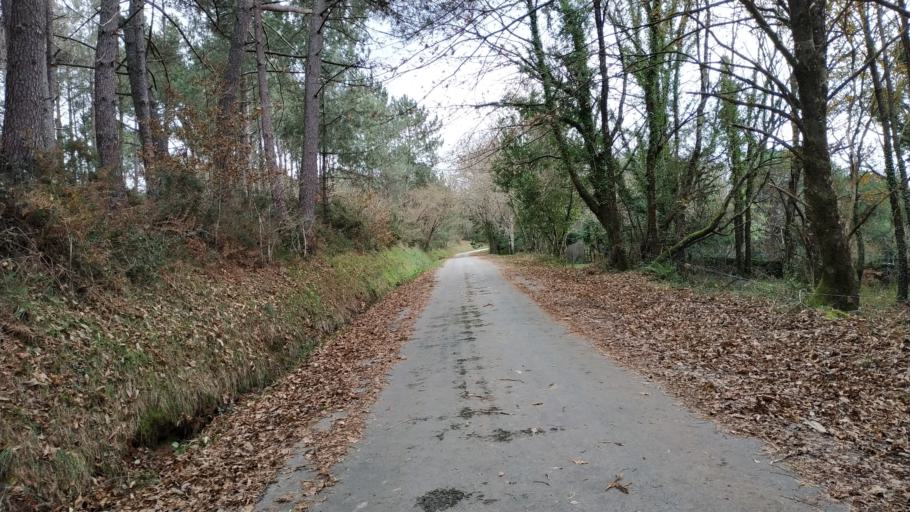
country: ES
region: Galicia
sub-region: Provincia de Pontevedra
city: Silleda
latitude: 42.7736
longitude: -8.1686
